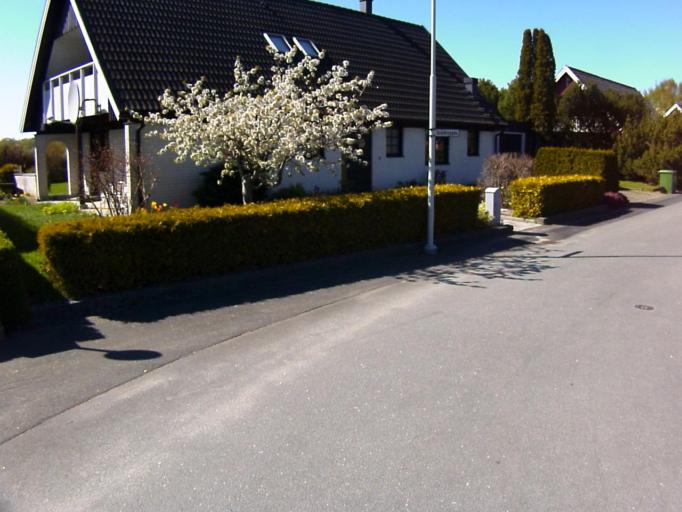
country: SE
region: Skane
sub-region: Kristianstads Kommun
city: Kristianstad
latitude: 56.0323
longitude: 14.1942
